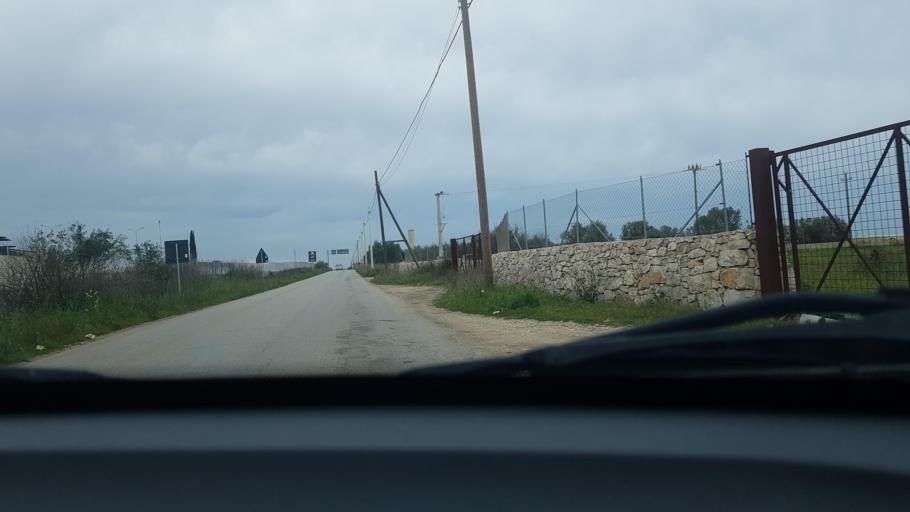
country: IT
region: Apulia
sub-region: Provincia di Bari
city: Noicattaro
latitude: 41.0333
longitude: 16.9781
